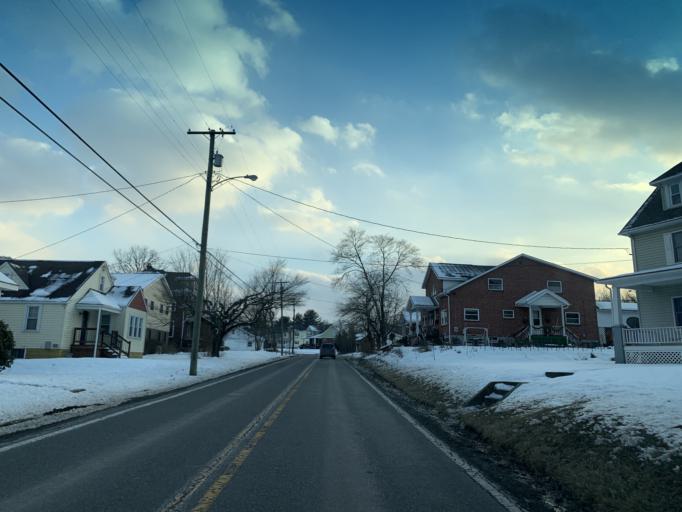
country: US
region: Maryland
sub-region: Allegany County
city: Cumberland
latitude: 39.7177
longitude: -78.7770
